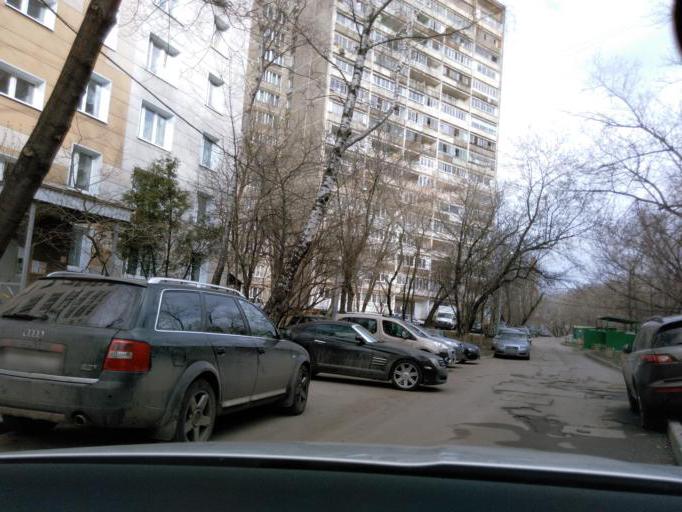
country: RU
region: Moscow
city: Novyye Cheremushki
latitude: 55.6928
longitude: 37.5957
